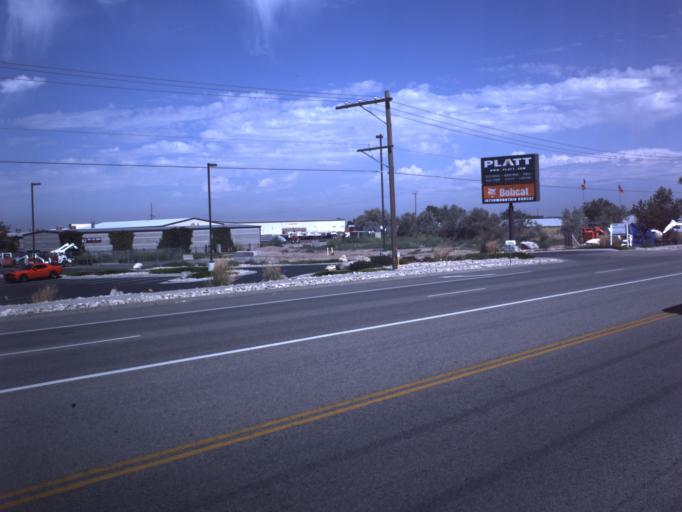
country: US
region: Utah
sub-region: Weber County
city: West Haven
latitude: 41.2101
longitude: -112.0257
